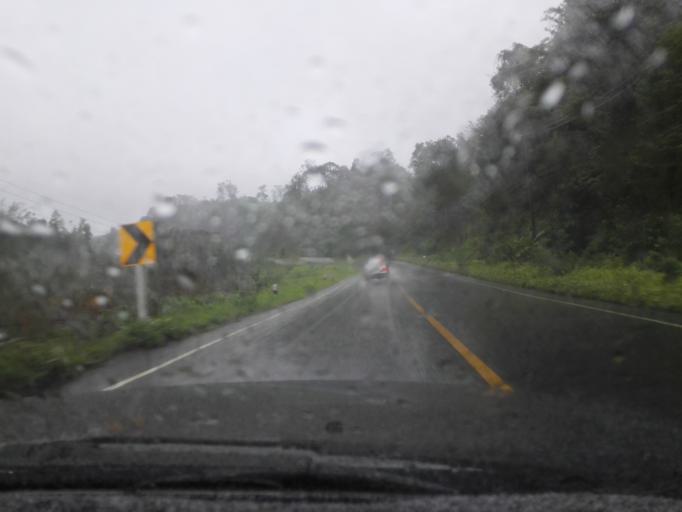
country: TH
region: Tak
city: Tak
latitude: 16.7789
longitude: 98.9392
